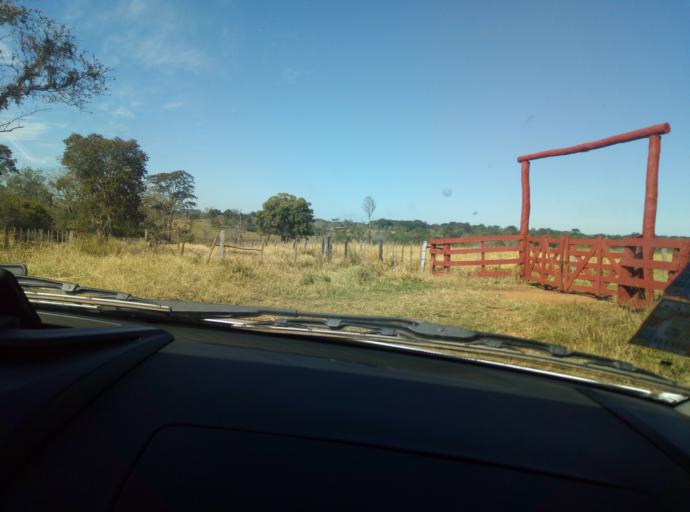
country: PY
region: Caaguazu
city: Carayao
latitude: -25.1766
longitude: -56.3010
